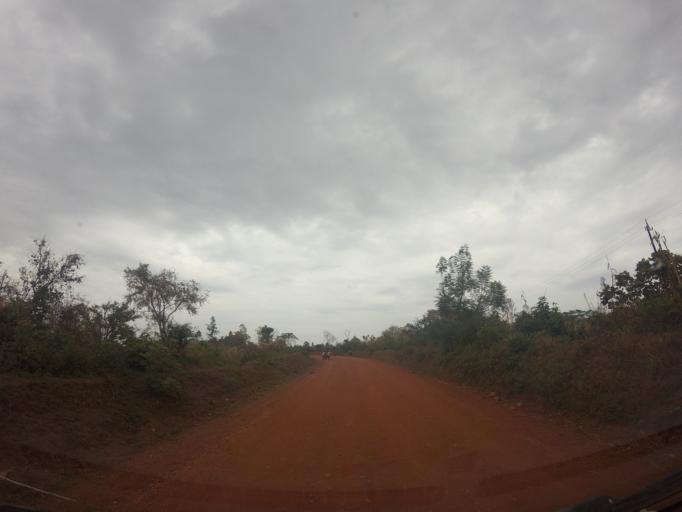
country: UG
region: Northern Region
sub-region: Arua District
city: Arua
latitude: 2.7703
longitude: 30.8601
